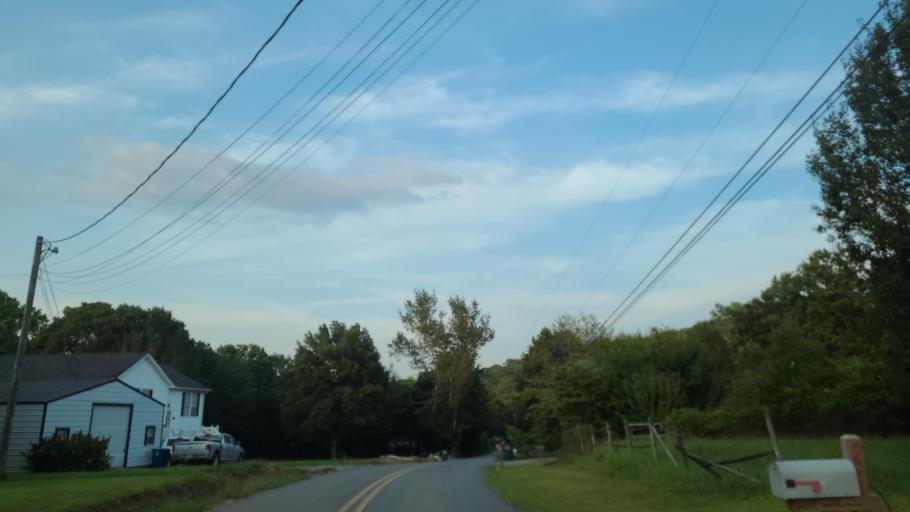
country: US
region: Georgia
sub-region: Bartow County
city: Adairsville
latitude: 34.4254
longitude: -84.9108
